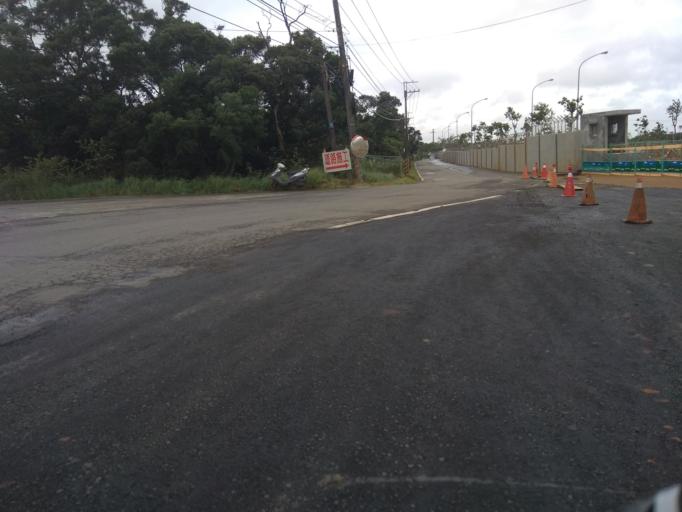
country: TW
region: Taiwan
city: Daxi
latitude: 24.9419
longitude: 121.1822
